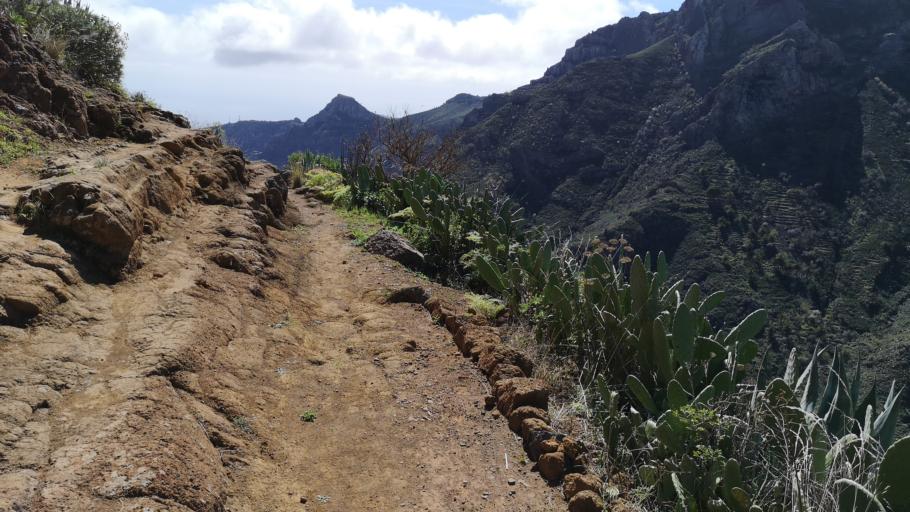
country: ES
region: Canary Islands
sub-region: Provincia de Santa Cruz de Tenerife
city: Alajero
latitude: 28.0838
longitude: -17.2329
